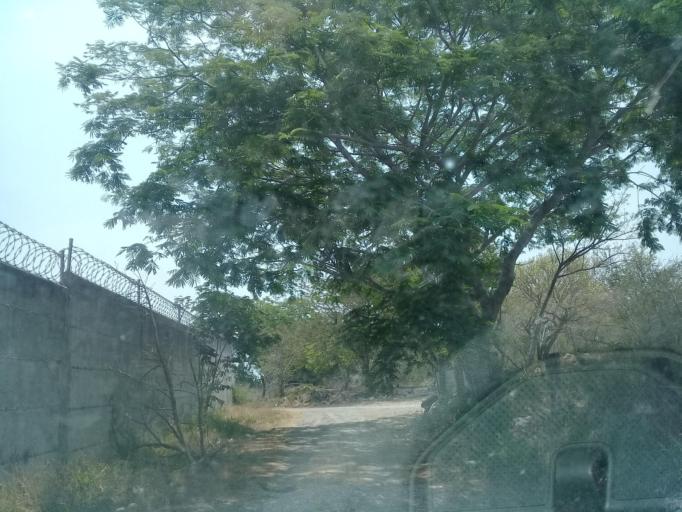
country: MX
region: Veracruz
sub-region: Veracruz
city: Hacienda Sotavento
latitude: 19.1349
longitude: -96.1824
